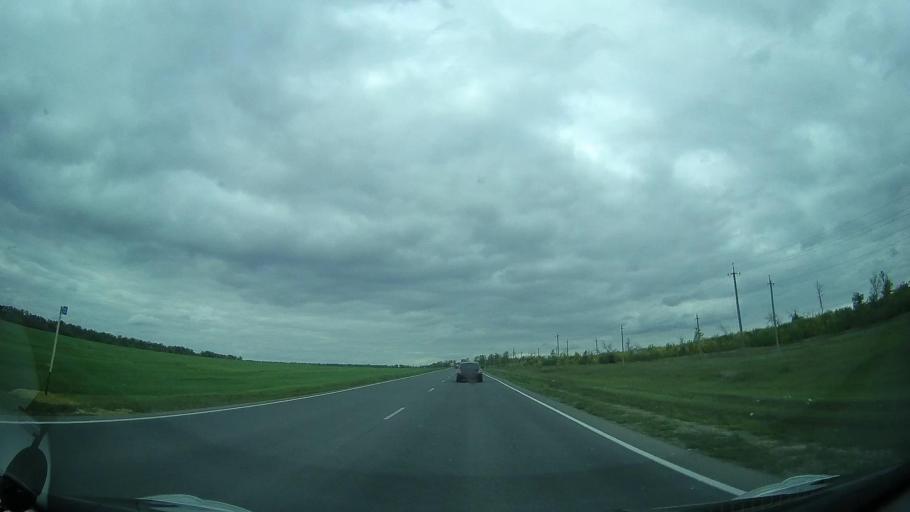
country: RU
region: Rostov
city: Yegorlykskaya
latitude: 46.5723
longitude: 40.6311
